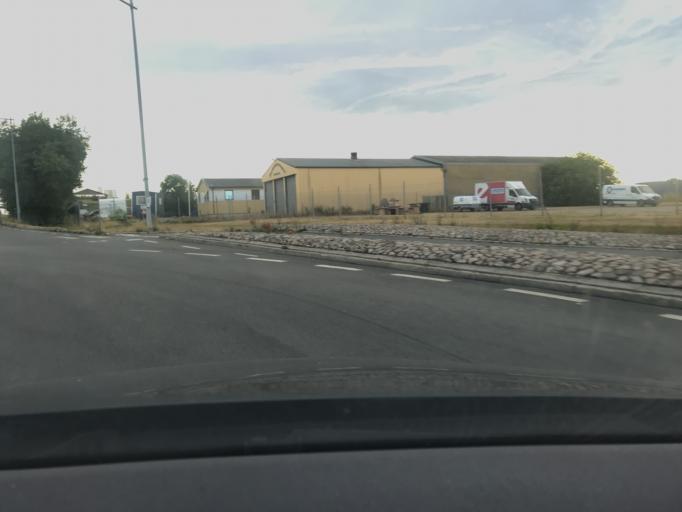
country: SE
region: Skane
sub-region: Simrishamns Kommun
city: Simrishamn
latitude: 55.5500
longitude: 14.3491
